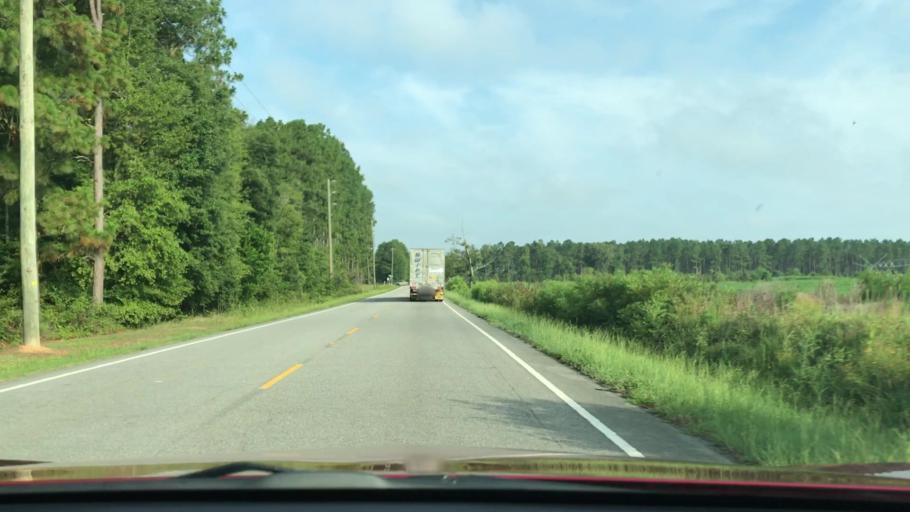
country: US
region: South Carolina
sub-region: Barnwell County
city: Williston
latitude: 33.6125
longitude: -81.2798
